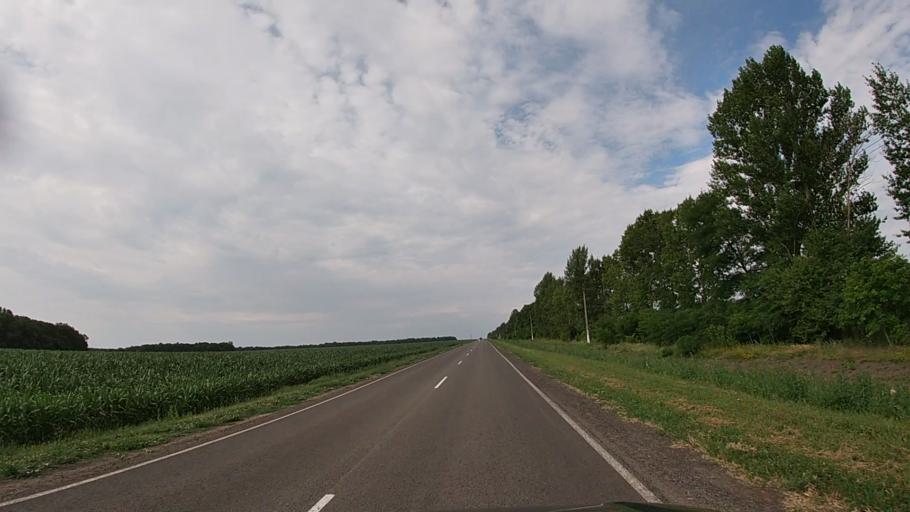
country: RU
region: Belgorod
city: Krasnaya Yaruga
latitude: 50.8274
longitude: 35.4722
